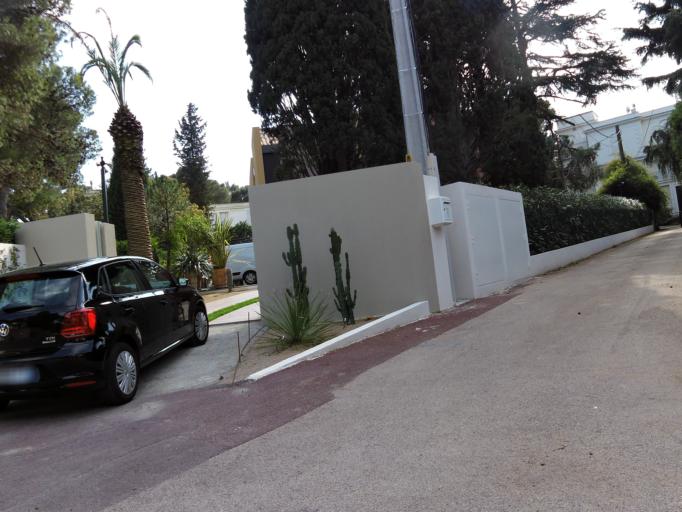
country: FR
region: Provence-Alpes-Cote d'Azur
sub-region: Departement des Alpes-Maritimes
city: Saint-Jean-Cap-Ferrat
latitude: 43.6886
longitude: 7.3251
